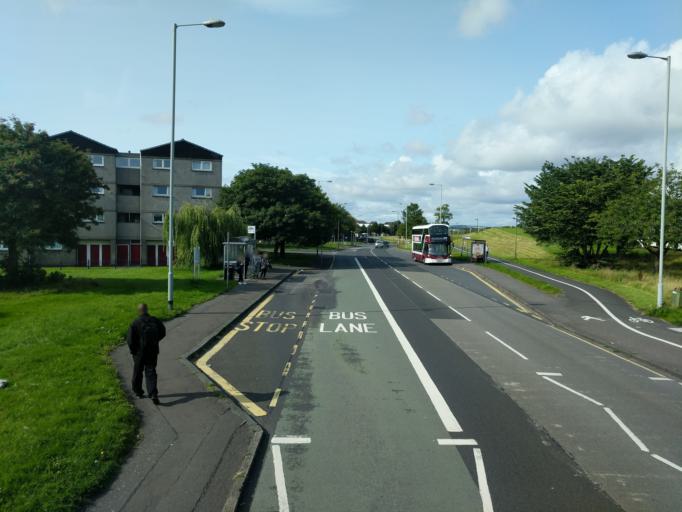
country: GB
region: Scotland
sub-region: Edinburgh
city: Colinton
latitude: 55.9327
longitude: -3.2710
